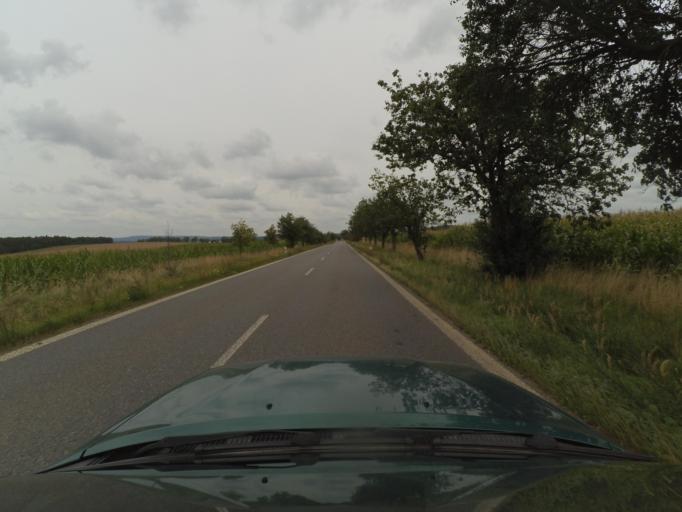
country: CZ
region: Central Bohemia
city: Rakovnik
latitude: 50.0798
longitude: 13.7178
